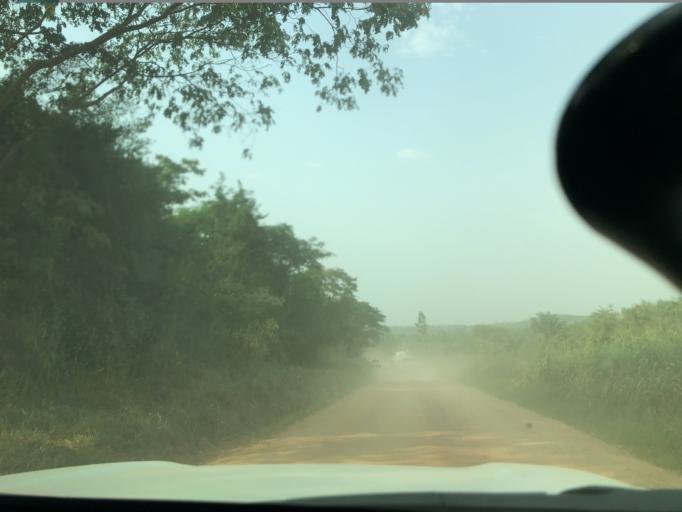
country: UG
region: Western Region
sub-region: Kasese District
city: Margherita
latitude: 0.1790
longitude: 29.6588
